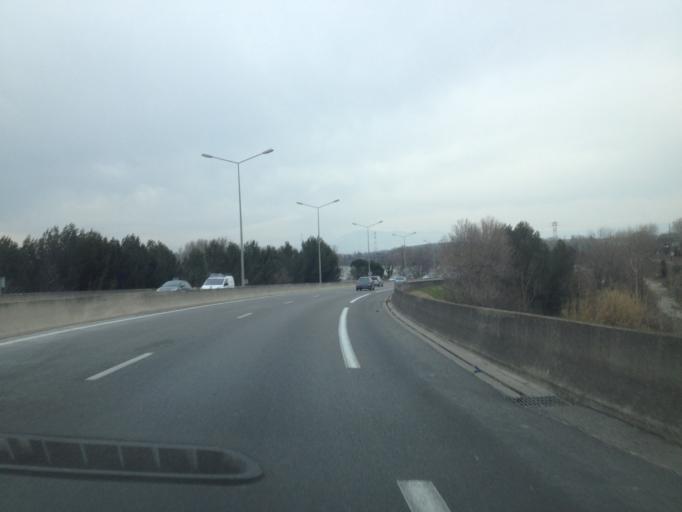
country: FR
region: Provence-Alpes-Cote d'Azur
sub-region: Departement du Vaucluse
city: Le Pontet
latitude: 43.9576
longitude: 4.8400
